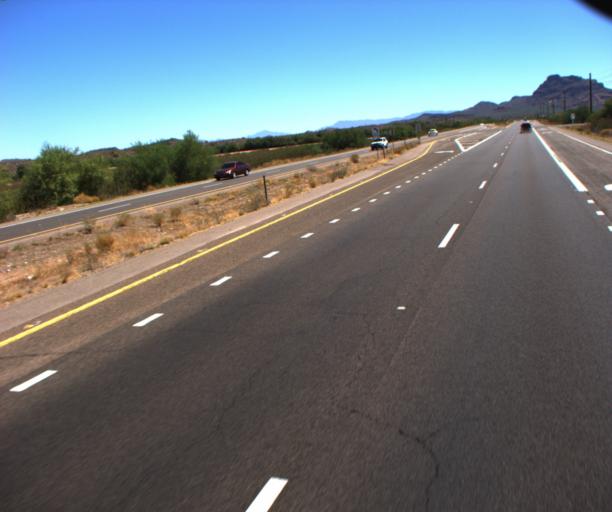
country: US
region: Arizona
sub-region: Maricopa County
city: Fountain Hills
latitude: 33.5122
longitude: -111.7588
